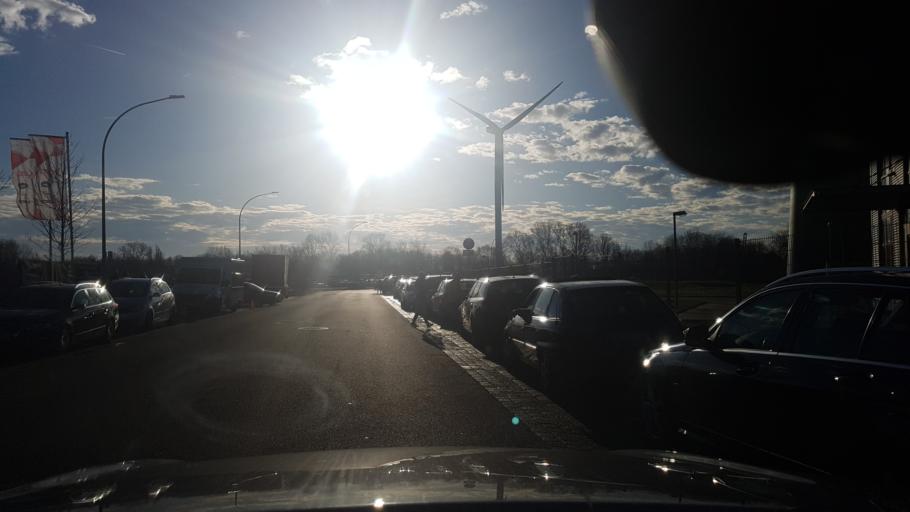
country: DE
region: Lower Saxony
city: Langen
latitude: 53.5952
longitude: 8.5495
